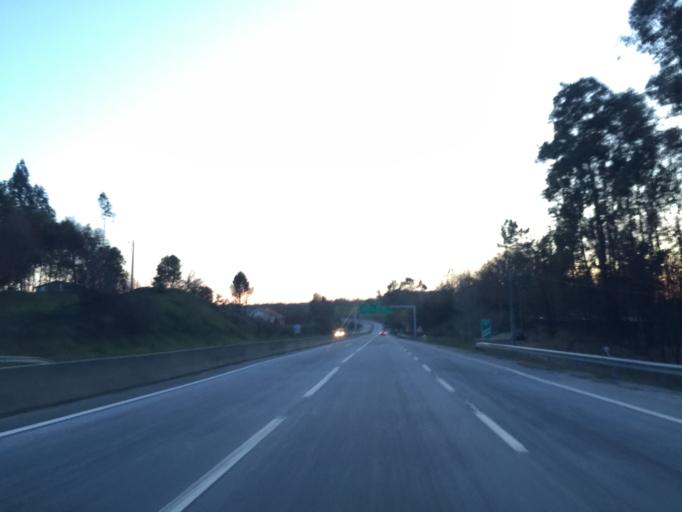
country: PT
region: Viseu
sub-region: Santa Comba Dao
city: Santa Comba Dao
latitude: 40.3864
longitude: -8.1135
